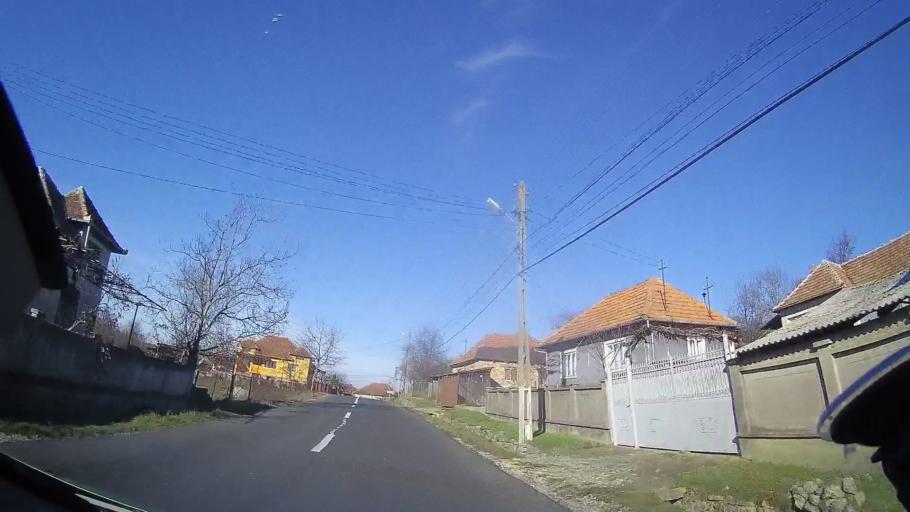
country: RO
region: Bihor
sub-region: Comuna Bratca
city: Beznea
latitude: 46.9696
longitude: 22.6136
